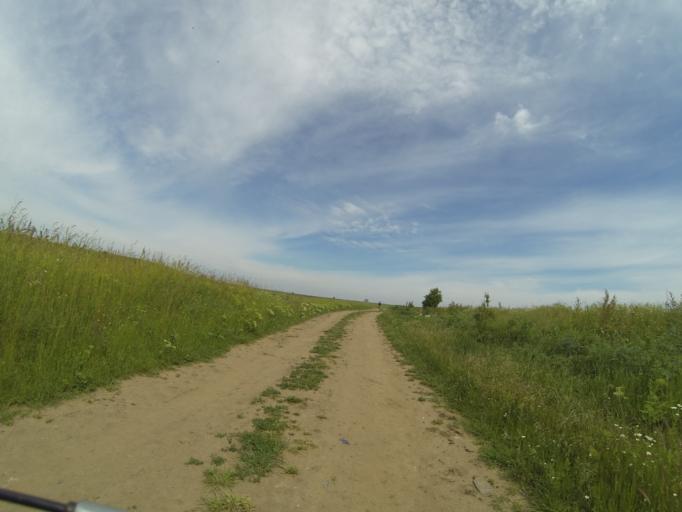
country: RO
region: Dolj
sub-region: Comuna Leu
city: Leu
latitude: 44.2024
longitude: 23.9934
